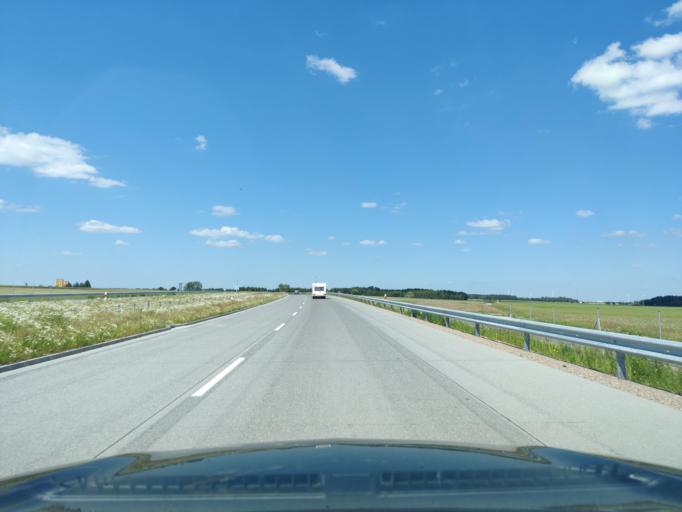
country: PL
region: Masovian Voivodeship
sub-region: Powiat mlawski
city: Wisniewo
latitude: 52.9953
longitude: 20.3460
